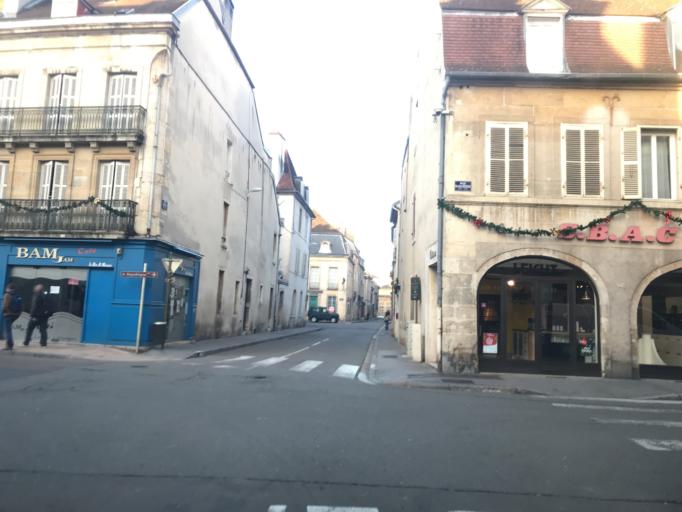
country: FR
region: Bourgogne
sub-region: Departement de la Cote-d'Or
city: Dijon
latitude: 47.3245
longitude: 5.0446
